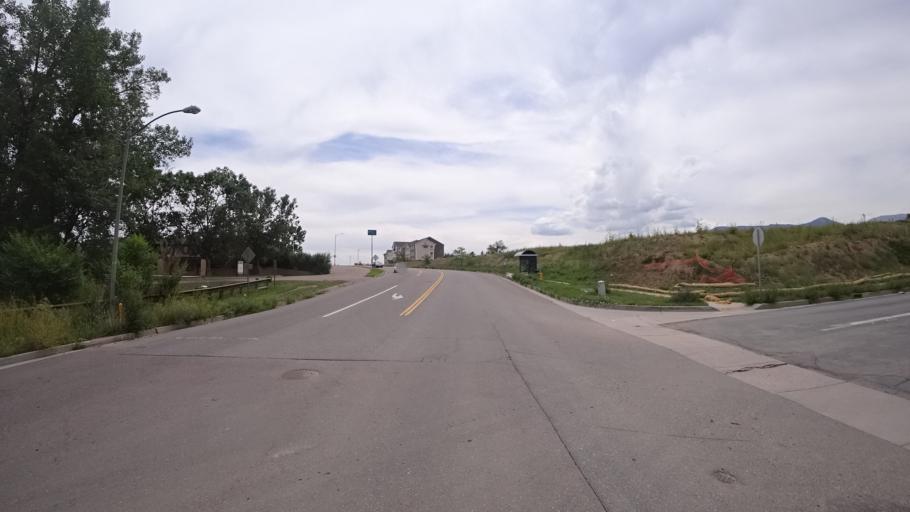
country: US
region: Colorado
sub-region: El Paso County
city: Colorado Springs
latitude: 38.8834
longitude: -104.8371
